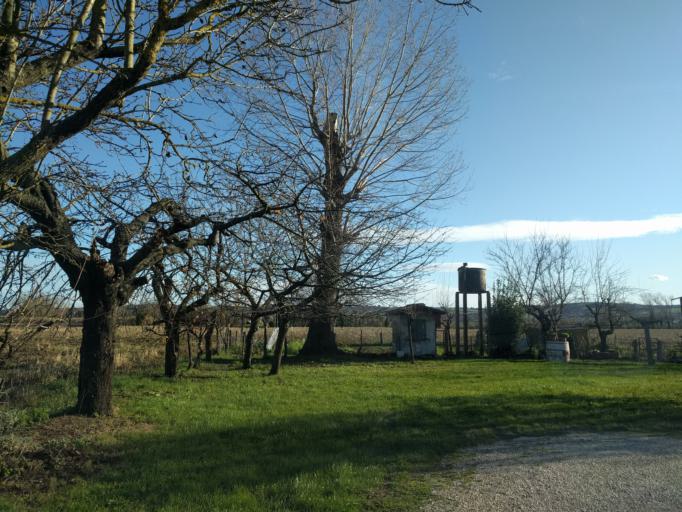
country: IT
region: The Marches
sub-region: Provincia di Pesaro e Urbino
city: Lucrezia
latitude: 43.7811
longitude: 12.9515
